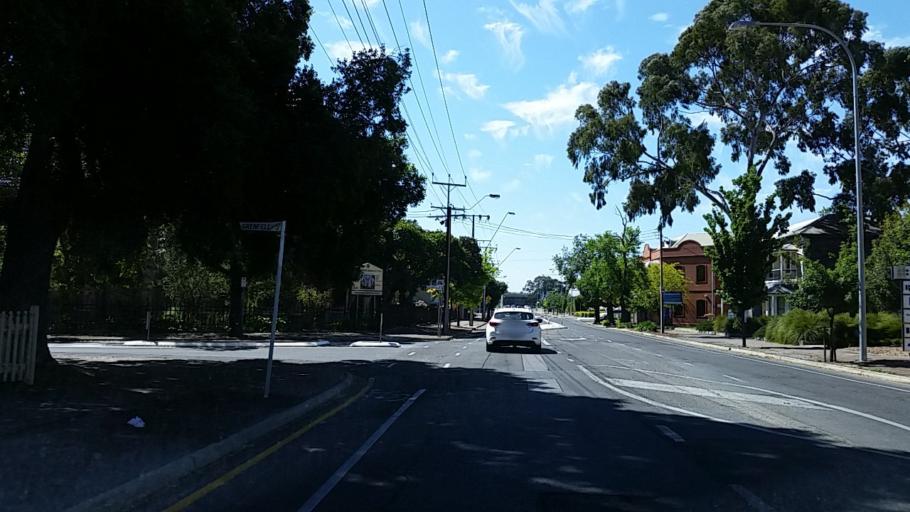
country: AU
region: South Australia
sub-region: Norwood Payneham St Peters
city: Trinity Gardens
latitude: -34.9197
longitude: 138.6230
